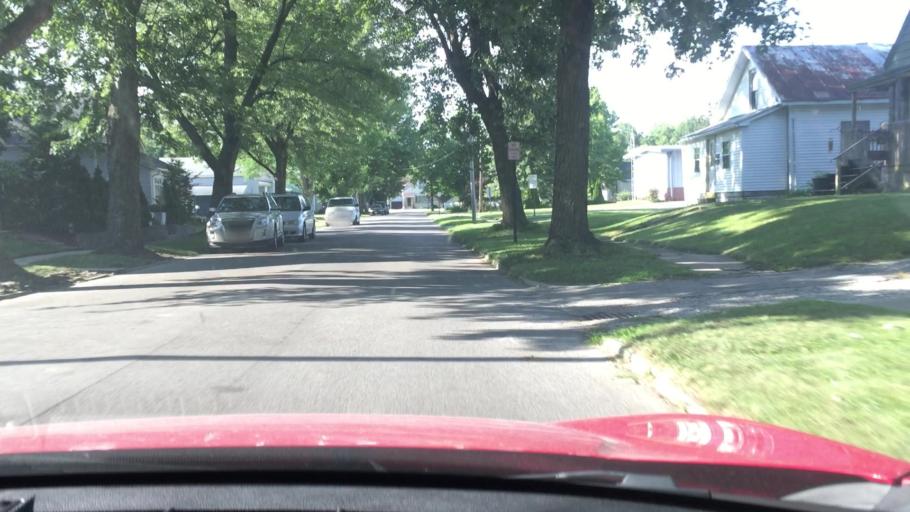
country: US
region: Ohio
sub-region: Hardin County
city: Ada
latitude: 40.7752
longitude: -83.8246
